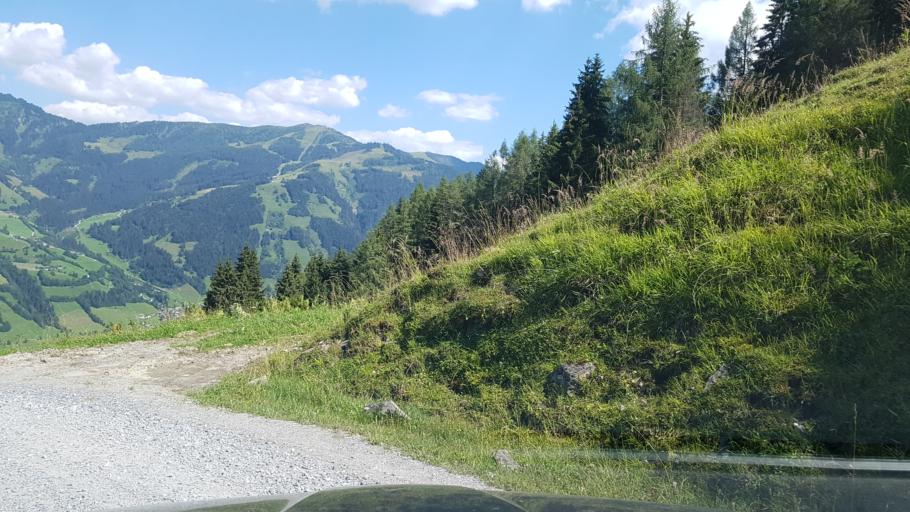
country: AT
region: Salzburg
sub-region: Politischer Bezirk Sankt Johann im Pongau
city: Dorfgastein
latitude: 47.2496
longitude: 13.0750
